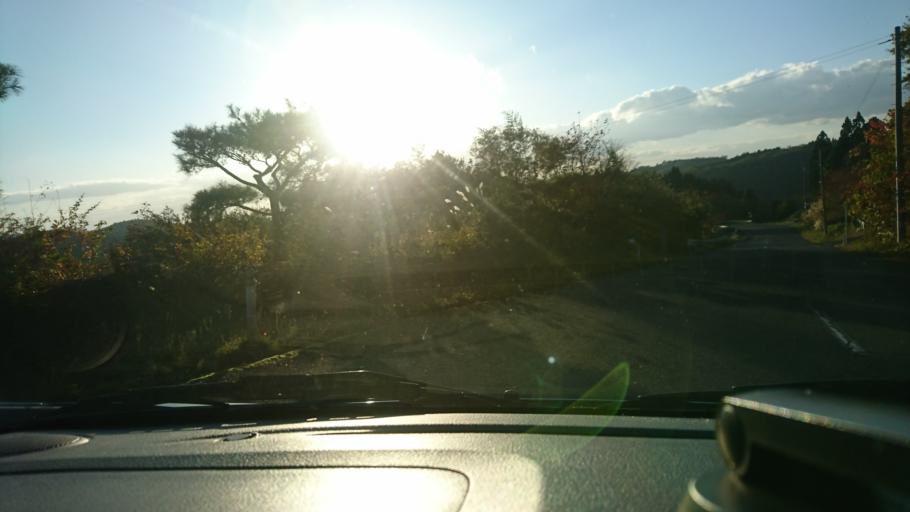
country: JP
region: Iwate
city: Ichinoseki
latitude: 38.7984
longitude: 141.2564
